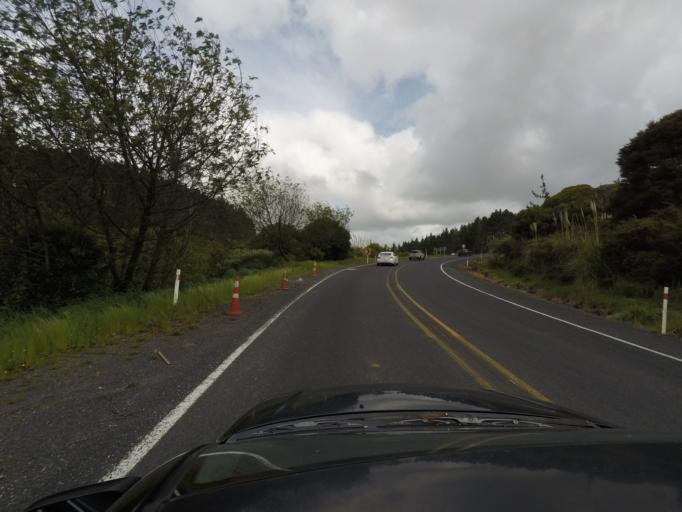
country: NZ
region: Auckland
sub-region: Auckland
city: Pakuranga
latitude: -36.9247
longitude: 174.9357
